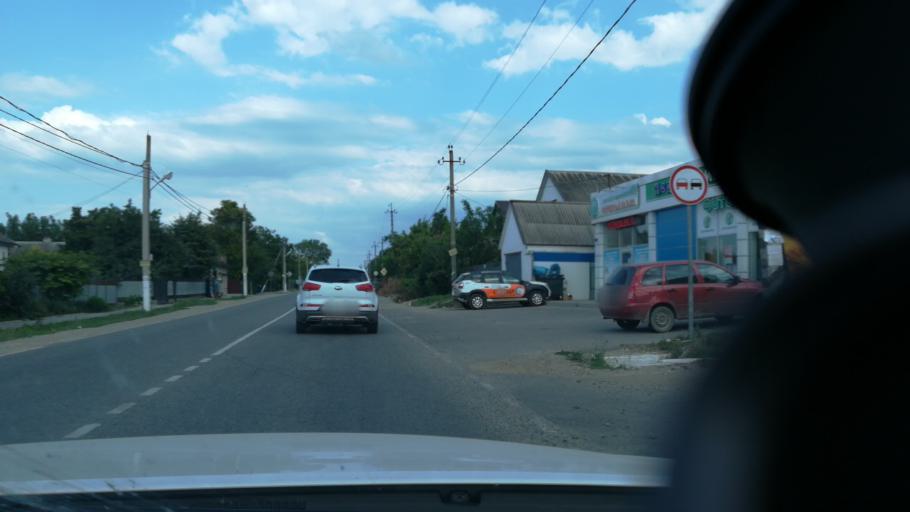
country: RU
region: Krasnodarskiy
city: Gostagayevskaya
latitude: 45.0258
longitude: 37.4976
